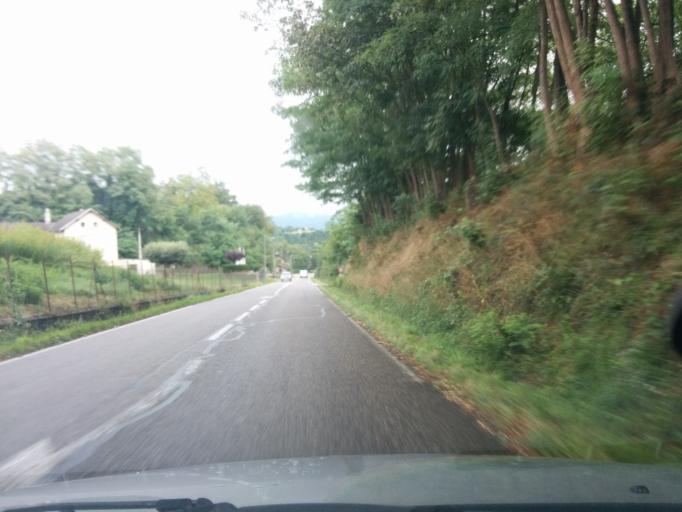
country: FR
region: Rhone-Alpes
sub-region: Departement de la Savoie
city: Le Pont-de-Beauvoisin
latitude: 45.5423
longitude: 5.6643
